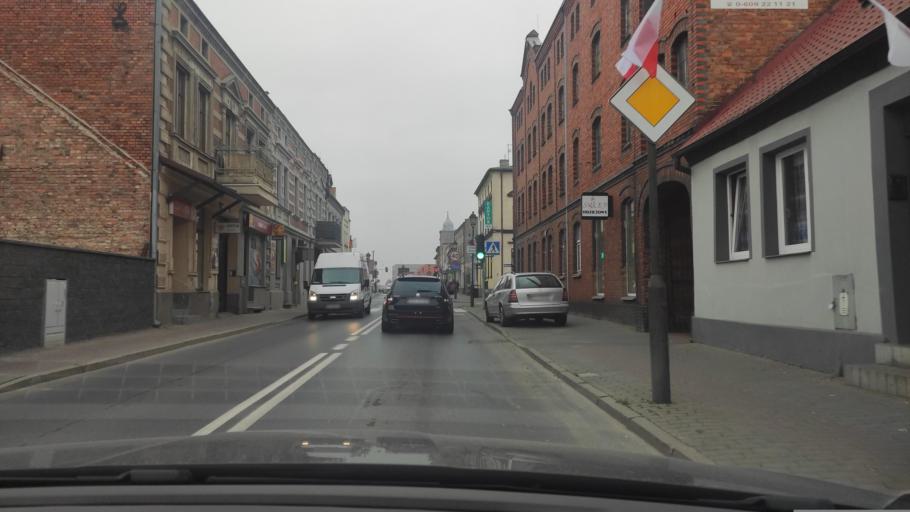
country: PL
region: Greater Poland Voivodeship
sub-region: Powiat poznanski
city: Kostrzyn
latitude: 52.3980
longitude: 17.2254
